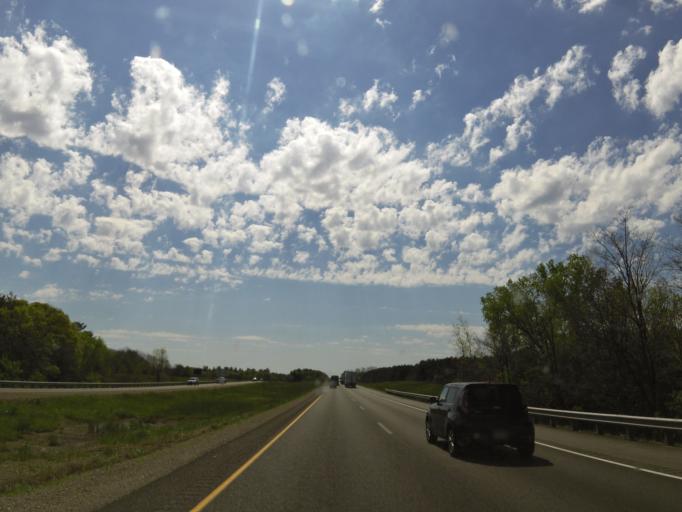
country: US
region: Wisconsin
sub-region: Eau Claire County
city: Altoona
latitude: 44.7564
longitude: -91.3950
